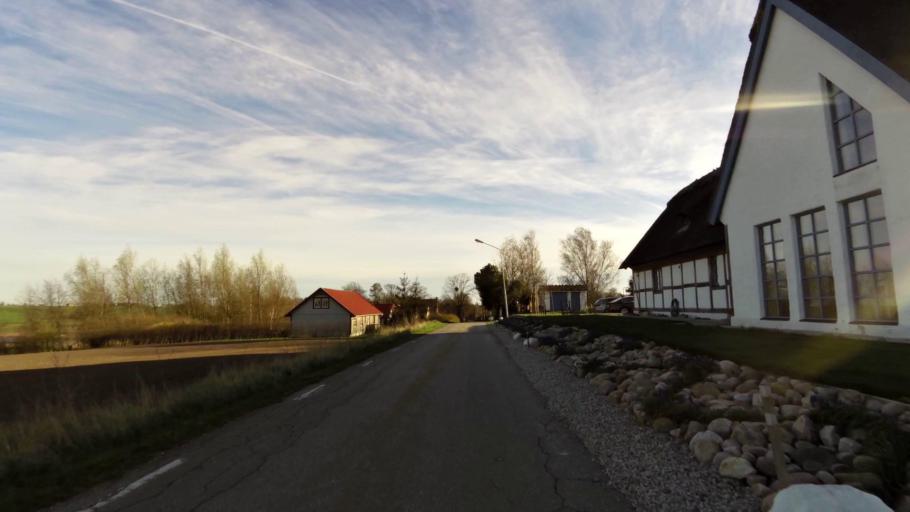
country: SE
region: Skane
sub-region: Kavlinge Kommun
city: Loddekopinge
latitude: 55.7712
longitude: 13.0555
